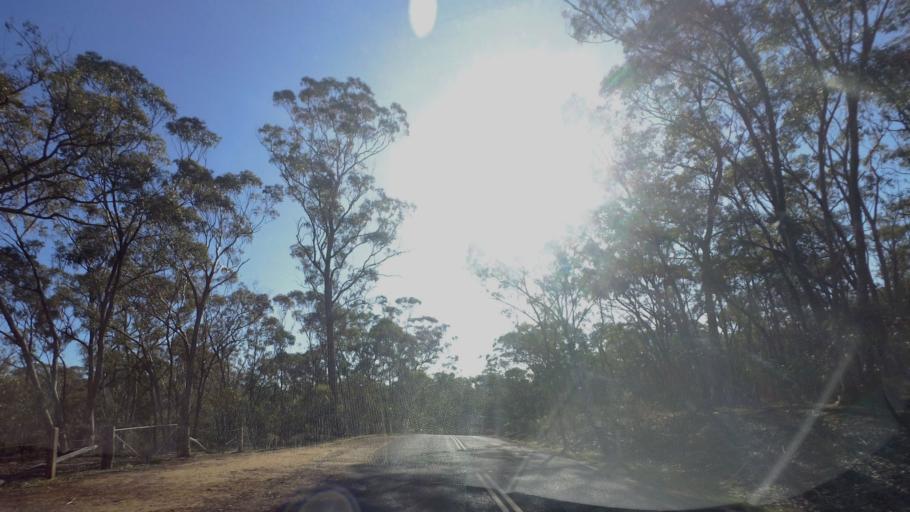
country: AU
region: Victoria
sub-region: Greater Bendigo
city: Kangaroo Flat
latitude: -36.8828
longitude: 144.2824
